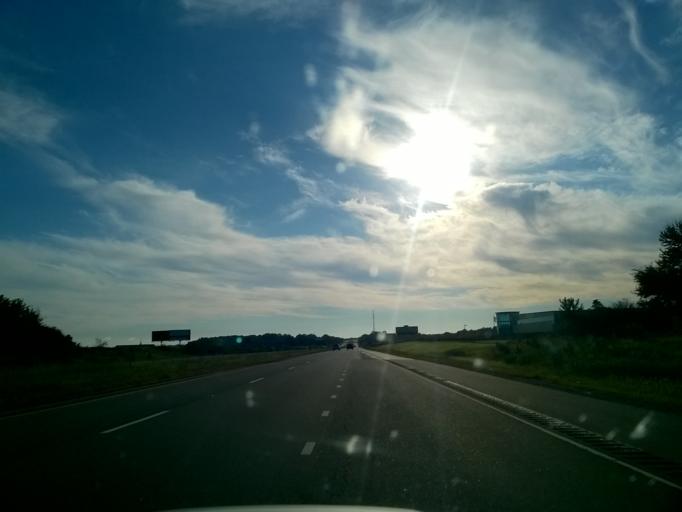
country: US
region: Indiana
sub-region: Gibson County
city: Haubstadt
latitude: 38.1696
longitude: -87.4612
